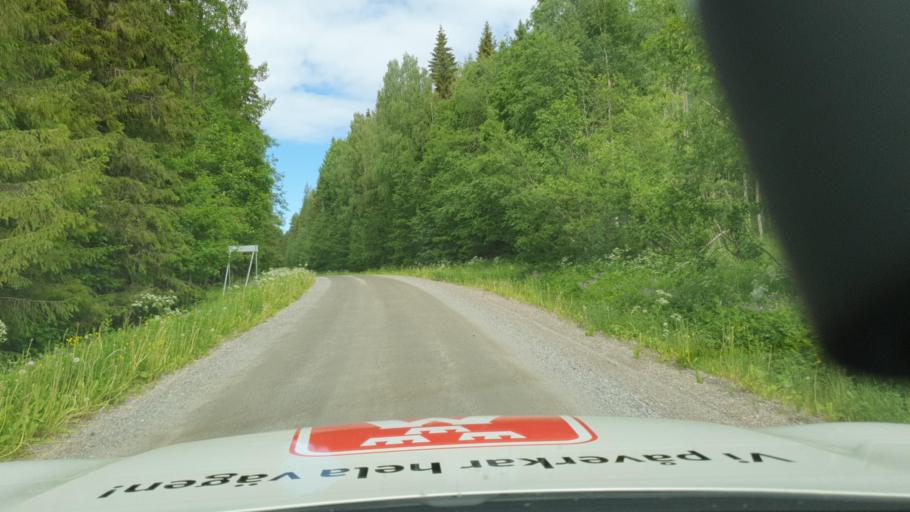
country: SE
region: Vaesterbotten
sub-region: Skelleftea Kommun
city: Forsbacka
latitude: 64.6393
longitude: 20.5448
